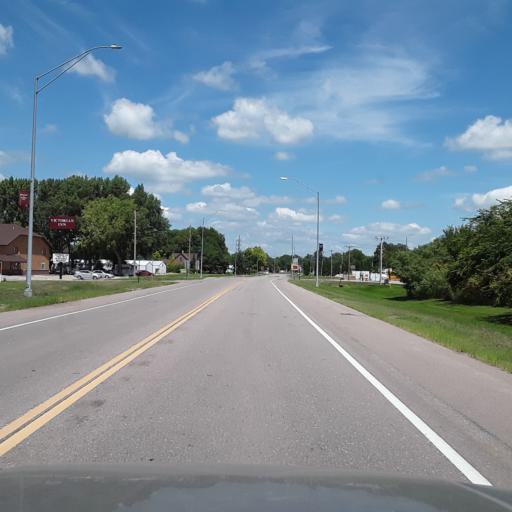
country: US
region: Nebraska
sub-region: Merrick County
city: Central City
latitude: 41.1015
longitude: -98.0014
